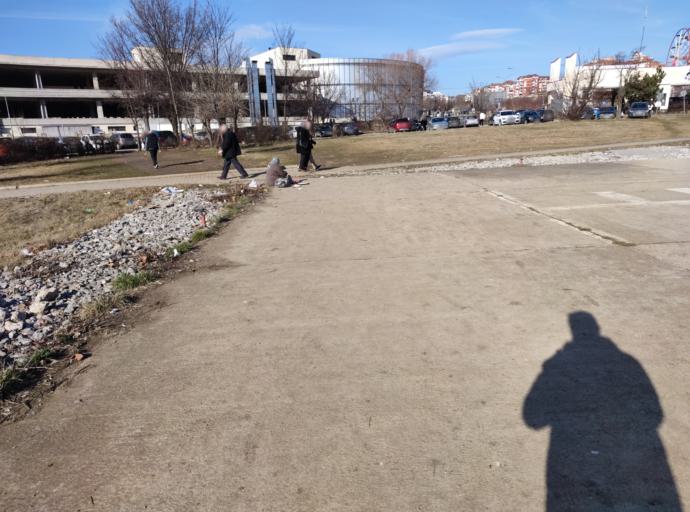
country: XK
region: Pristina
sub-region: Komuna e Prishtines
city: Pristina
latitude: 42.6459
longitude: 21.1626
